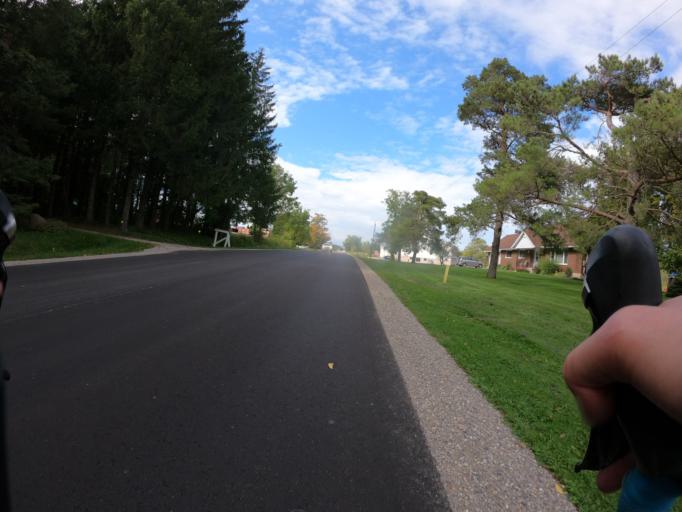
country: CA
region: Ontario
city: Kitchener
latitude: 43.3843
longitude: -80.6260
